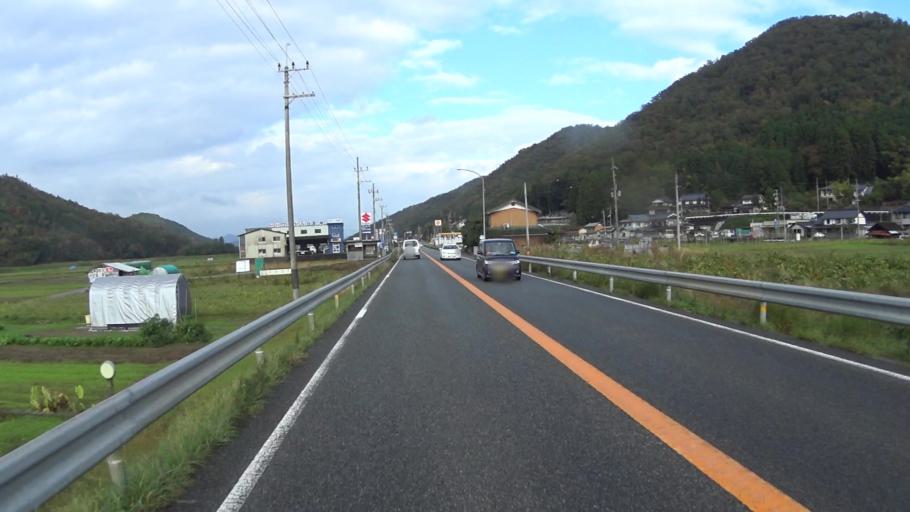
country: JP
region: Kyoto
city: Ayabe
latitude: 35.2534
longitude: 135.2061
